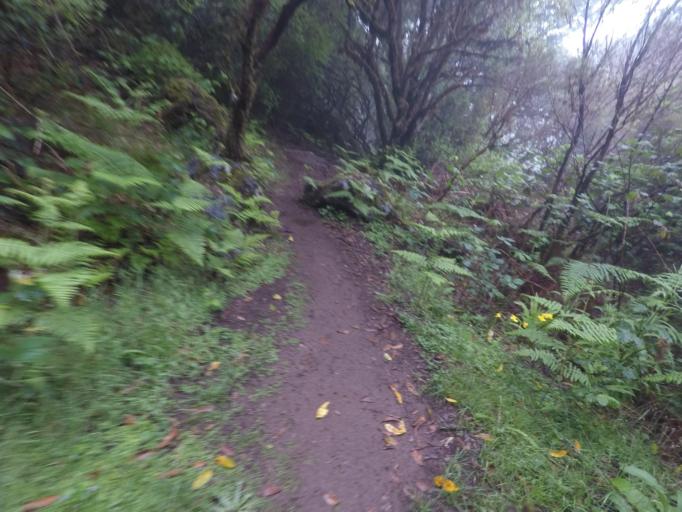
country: PT
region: Madeira
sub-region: Calheta
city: Arco da Calheta
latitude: 32.7730
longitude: -17.1197
